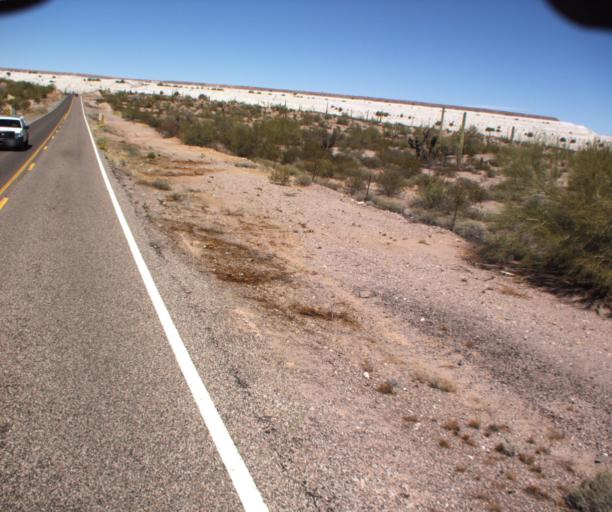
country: US
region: Arizona
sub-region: Pima County
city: Ajo
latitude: 32.3633
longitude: -112.8360
